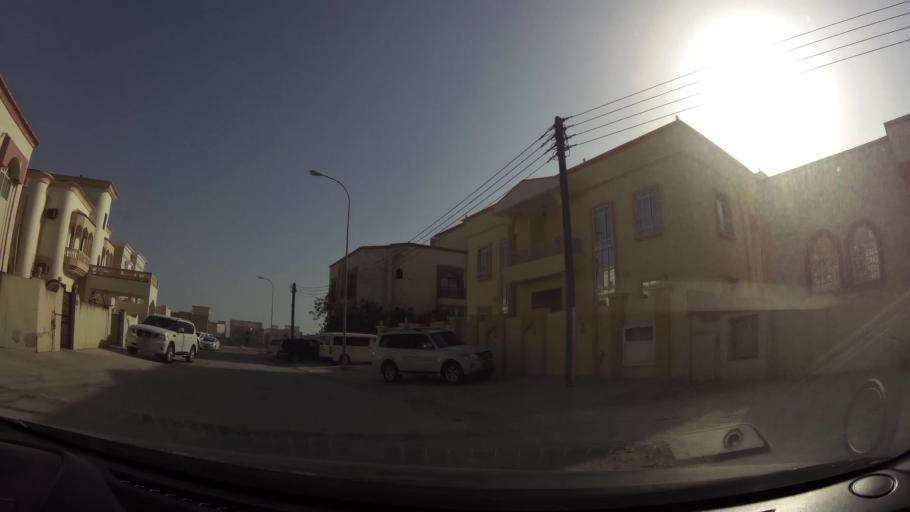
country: OM
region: Zufar
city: Salalah
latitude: 17.0156
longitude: 54.0169
